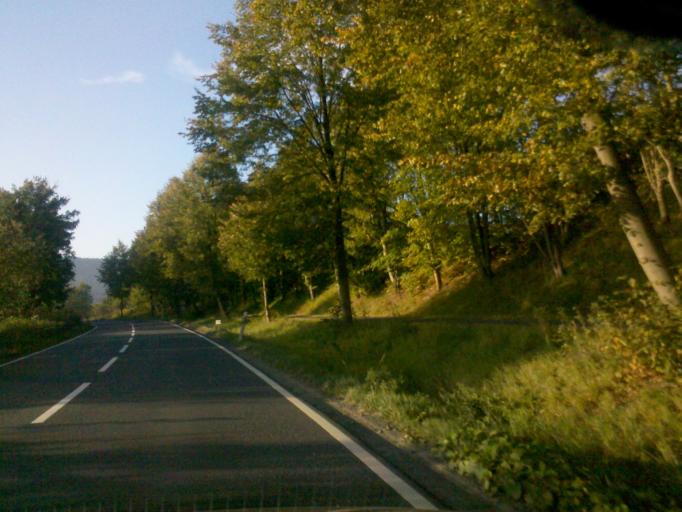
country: DE
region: Hesse
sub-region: Regierungsbezirk Giessen
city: Haiger
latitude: 50.7511
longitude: 8.2070
